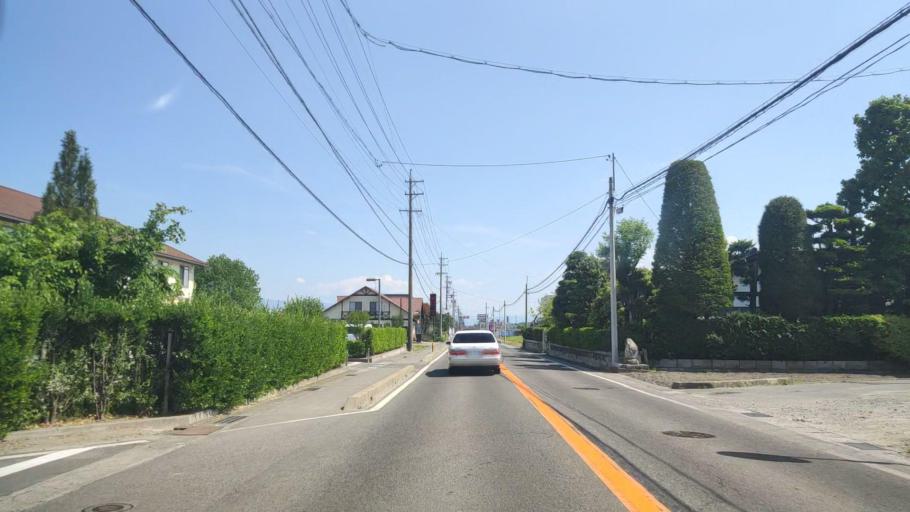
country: JP
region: Nagano
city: Hotaka
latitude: 36.3674
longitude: 137.8760
